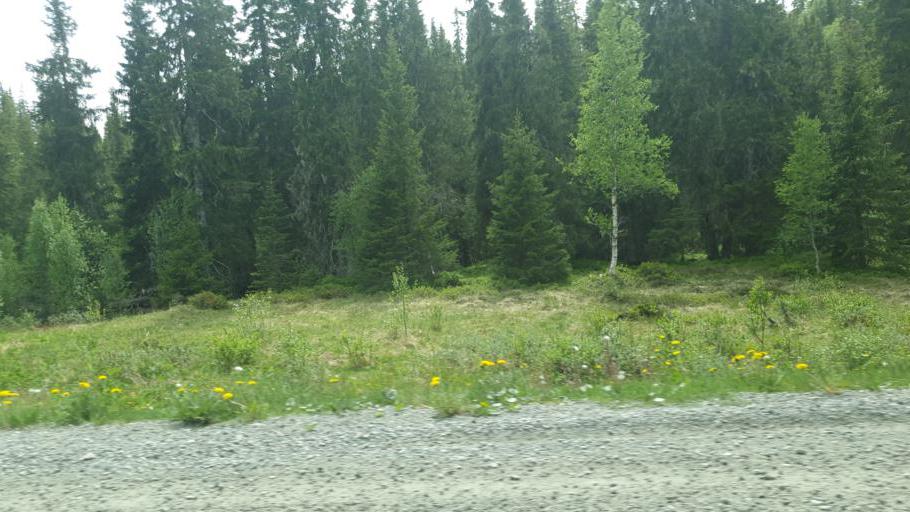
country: NO
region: Nord-Trondelag
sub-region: Leksvik
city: Leksvik
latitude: 63.6975
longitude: 10.4892
